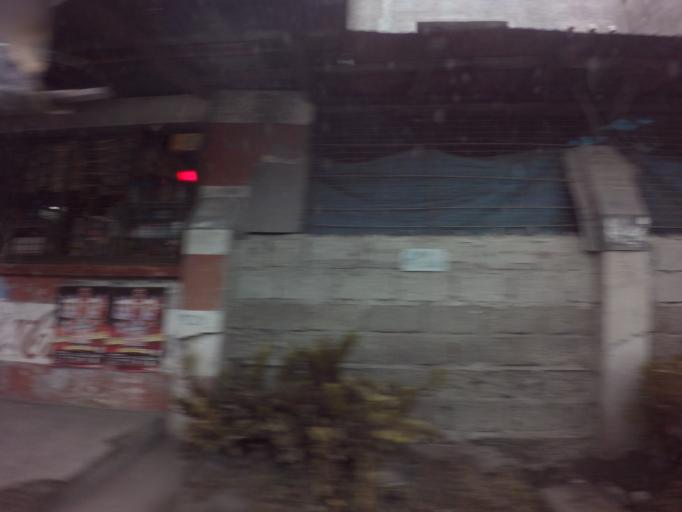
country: PH
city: Sambayanihan People's Village
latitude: 14.4324
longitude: 121.0501
